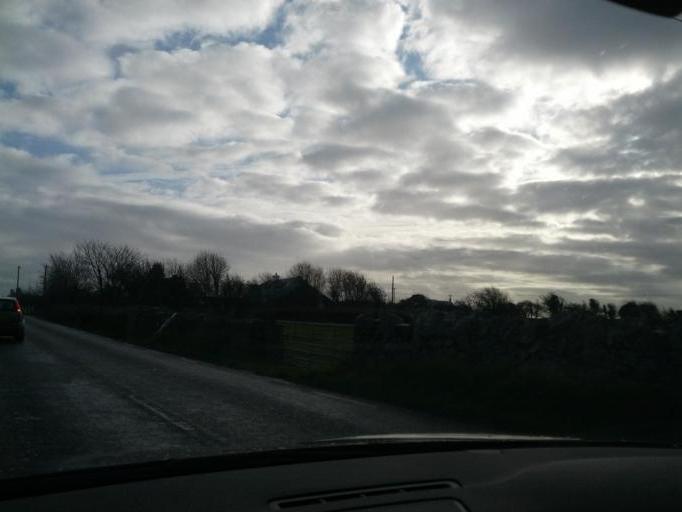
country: IE
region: Connaught
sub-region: County Galway
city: Oranmore
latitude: 53.3177
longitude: -8.8645
